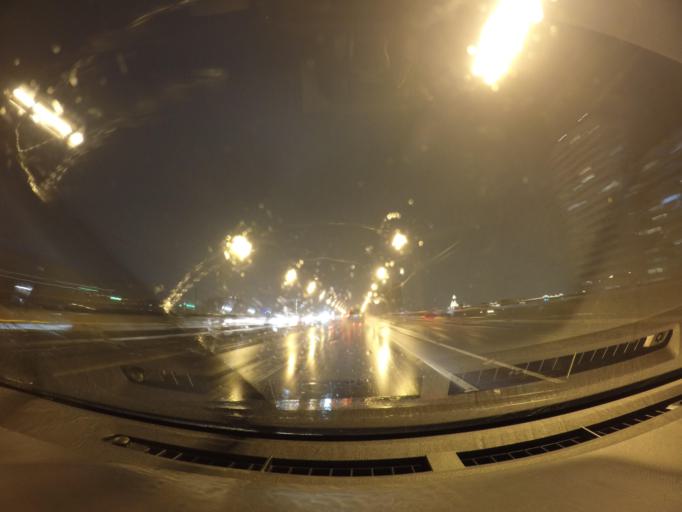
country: RU
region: Moskovskaya
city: Kozhukhovo
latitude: 55.6845
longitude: 37.6650
